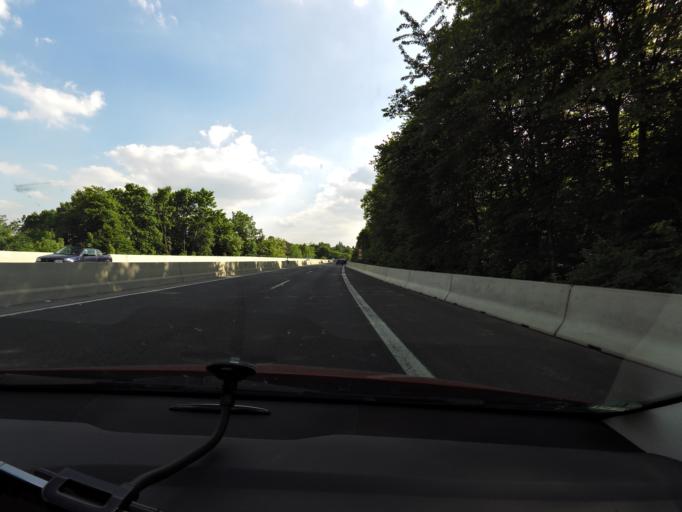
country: DE
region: Rheinland-Pfalz
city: Leutesdorf
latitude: 50.4388
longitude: 7.3920
